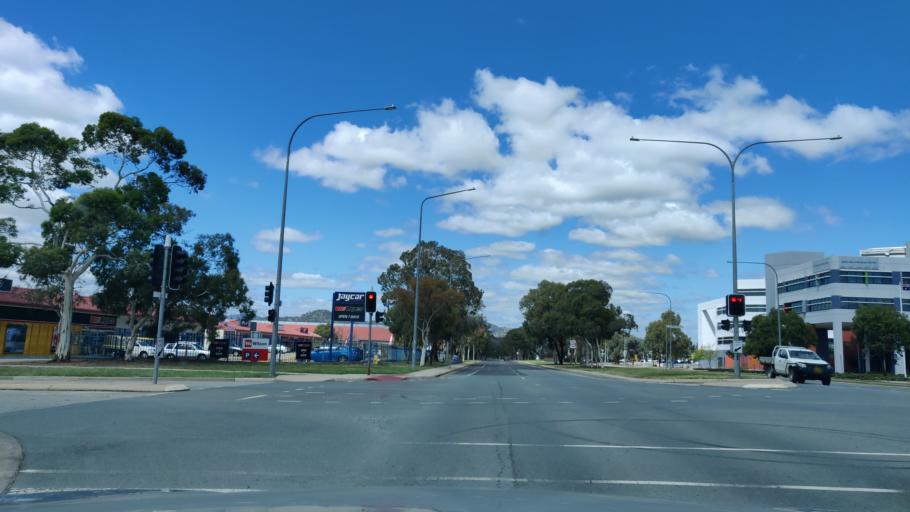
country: AU
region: Australian Capital Territory
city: Macarthur
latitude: -35.4197
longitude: 149.0655
